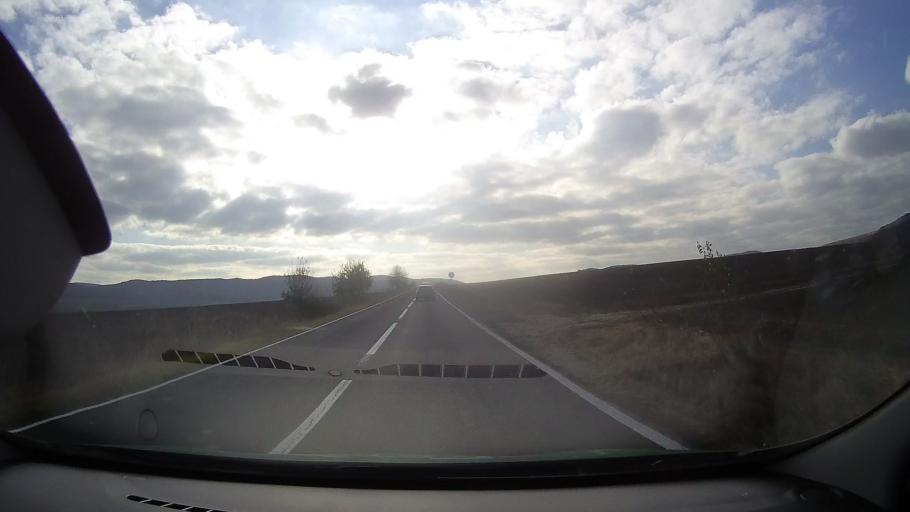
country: RO
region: Tulcea
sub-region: Comuna Nalbant
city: Nicolae Balcescu
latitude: 44.9822
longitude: 28.5508
